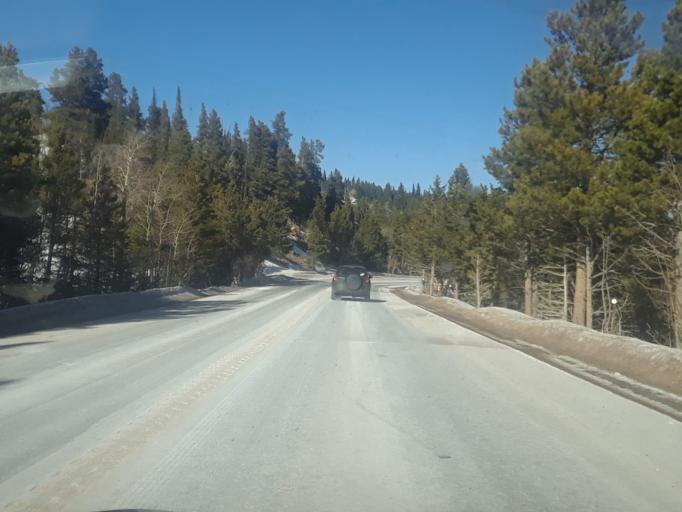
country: US
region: Colorado
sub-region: Boulder County
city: Nederland
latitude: 40.0887
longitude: -105.4959
